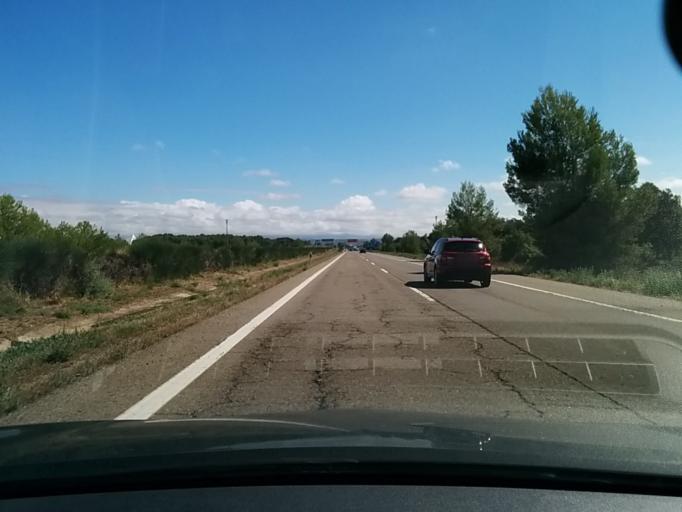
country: ES
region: Aragon
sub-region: Provincia de Huesca
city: Huesca
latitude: 42.1087
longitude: -0.4536
